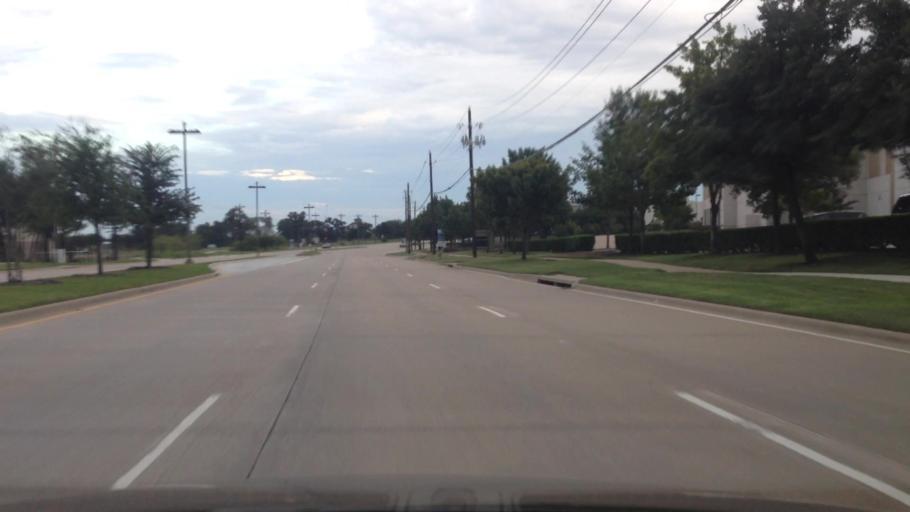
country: US
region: Texas
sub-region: Dallas County
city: Coppell
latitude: 32.9976
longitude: -97.0462
